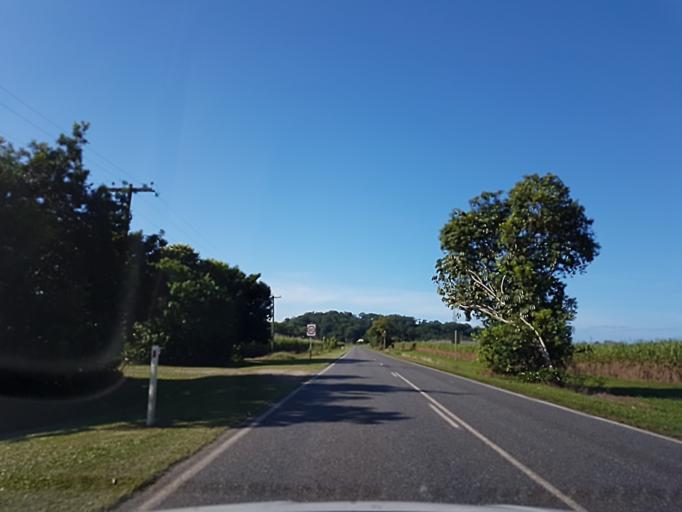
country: AU
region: Queensland
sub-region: Cairns
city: Port Douglas
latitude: -16.4394
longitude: 145.3771
